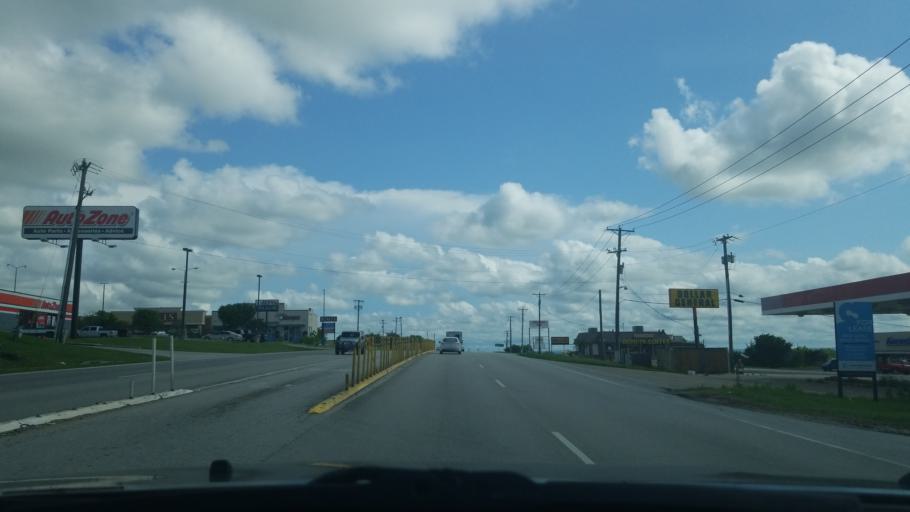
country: US
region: Texas
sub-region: Wise County
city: Decatur
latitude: 33.2257
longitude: -97.5947
